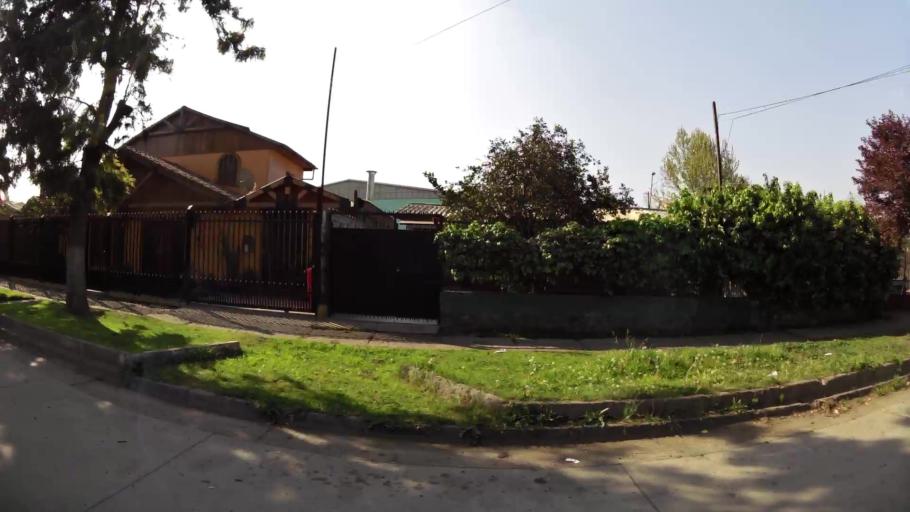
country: CL
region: Santiago Metropolitan
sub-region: Provincia de Santiago
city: Lo Prado
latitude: -33.3684
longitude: -70.6831
